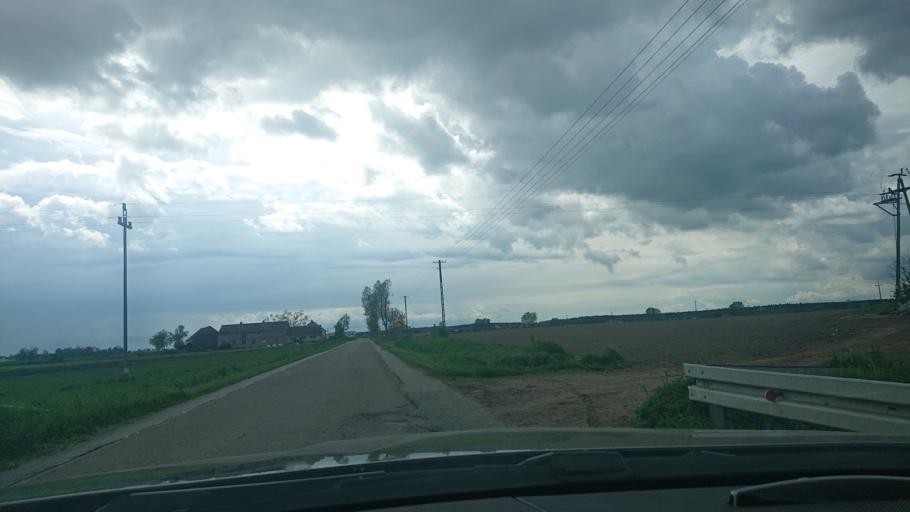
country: PL
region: Greater Poland Voivodeship
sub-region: Powiat gnieznienski
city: Niechanowo
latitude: 52.4773
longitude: 17.6440
